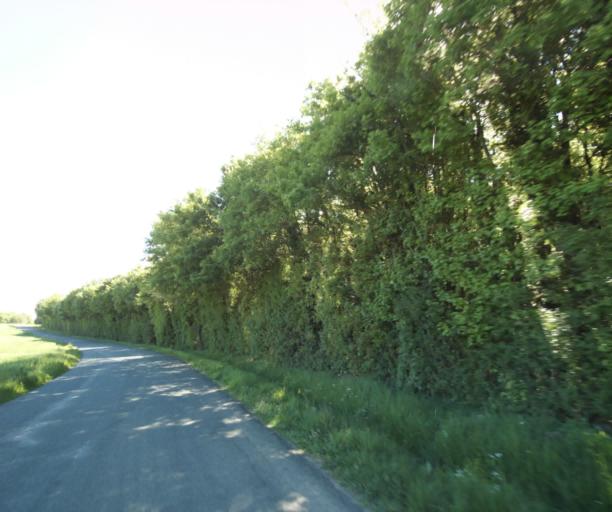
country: FR
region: Poitou-Charentes
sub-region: Departement de la Charente-Maritime
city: Bussac-sur-Charente
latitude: 45.8083
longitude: -0.6630
